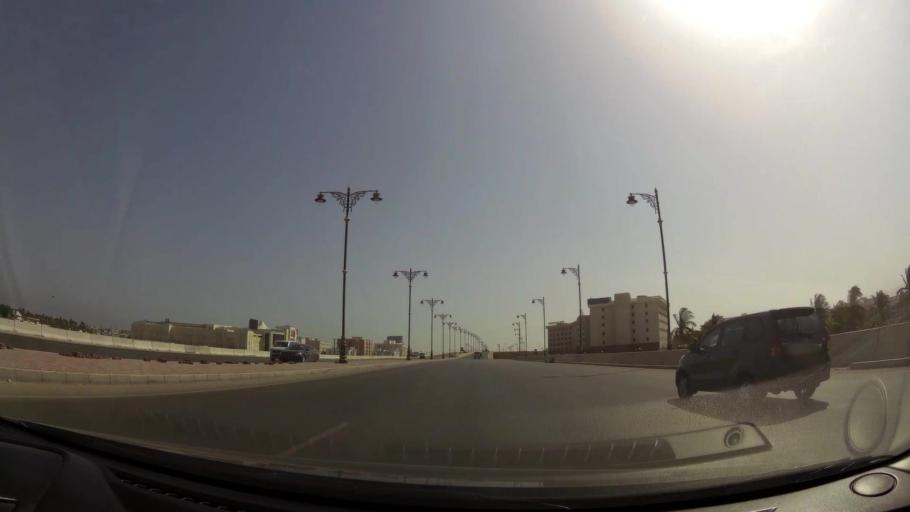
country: OM
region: Zufar
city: Salalah
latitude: 17.0200
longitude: 54.0633
